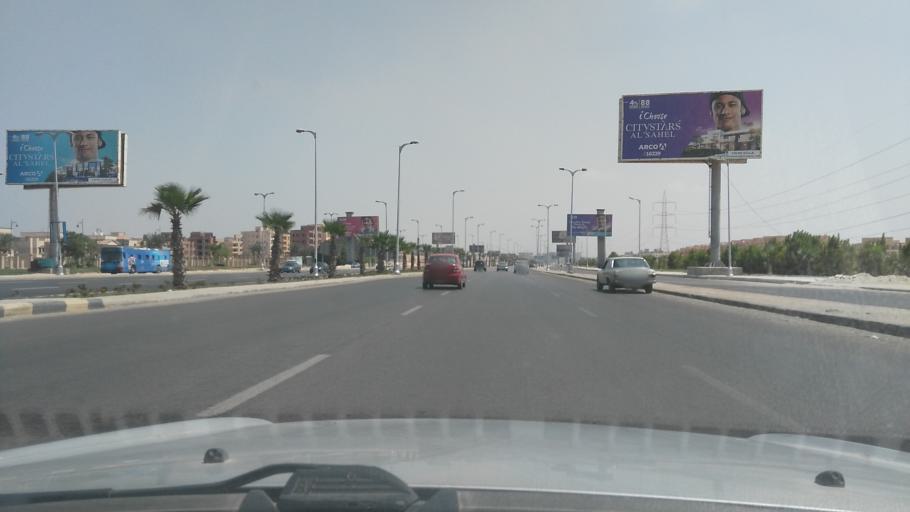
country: EG
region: Al Jizah
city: Awsim
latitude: 30.0367
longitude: 31.0349
